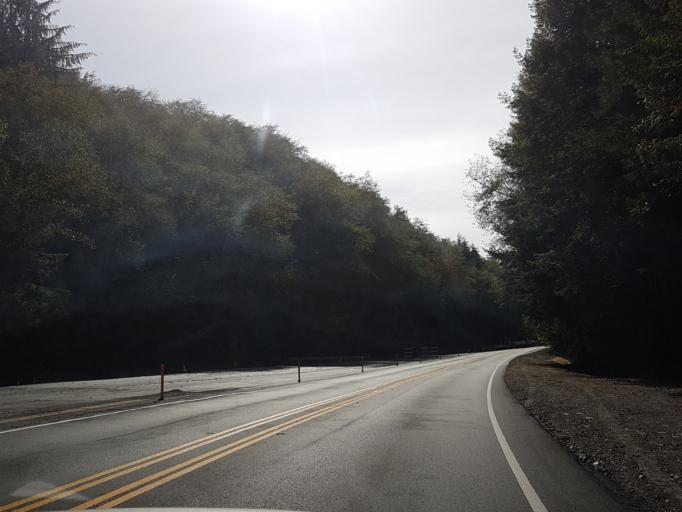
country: US
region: California
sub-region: Del Norte County
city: Bertsch-Oceanview
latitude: 41.4936
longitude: -124.0445
